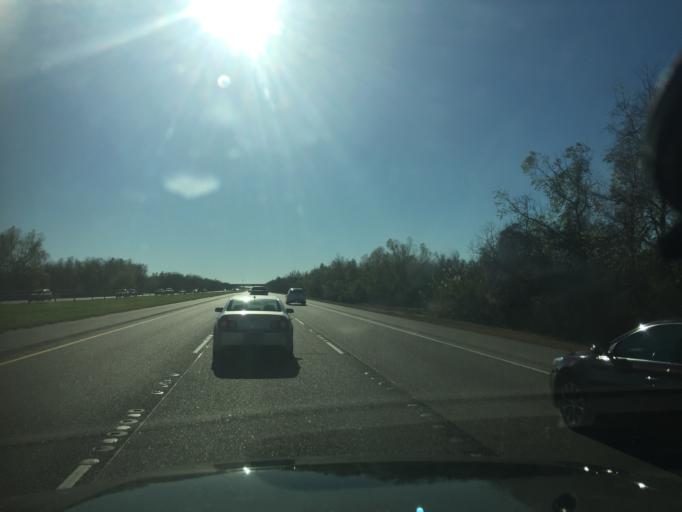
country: US
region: Louisiana
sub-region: Saint Tammany Parish
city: Eden Isle
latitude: 30.1138
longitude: -89.8898
